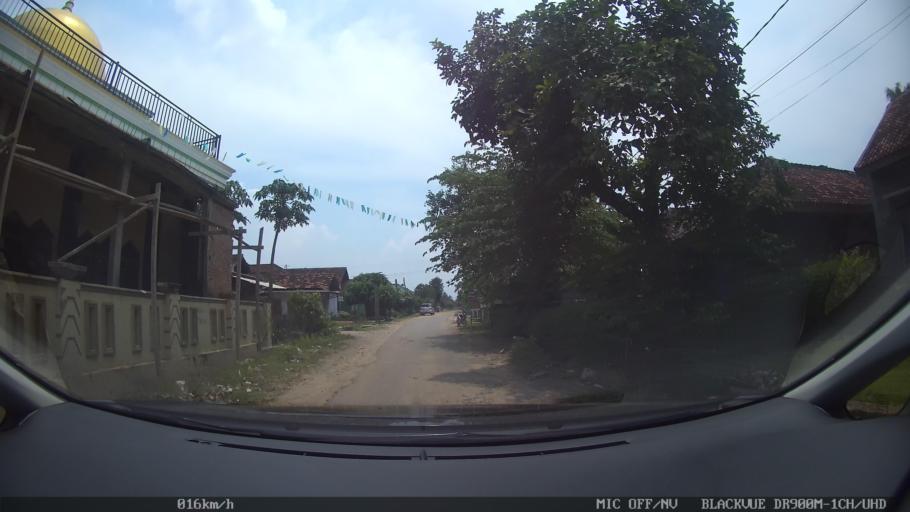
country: ID
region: Lampung
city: Natar
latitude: -5.3145
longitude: 105.2308
